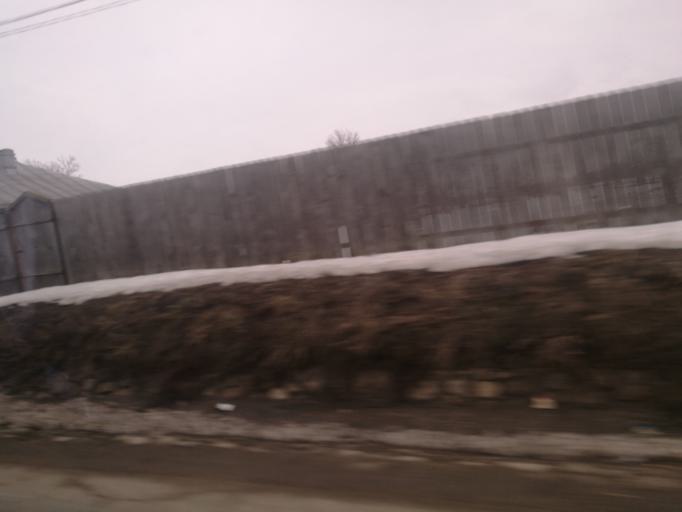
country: RO
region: Iasi
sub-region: Comuna Ruginoasa
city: Dumbravita
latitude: 47.2398
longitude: 26.8314
